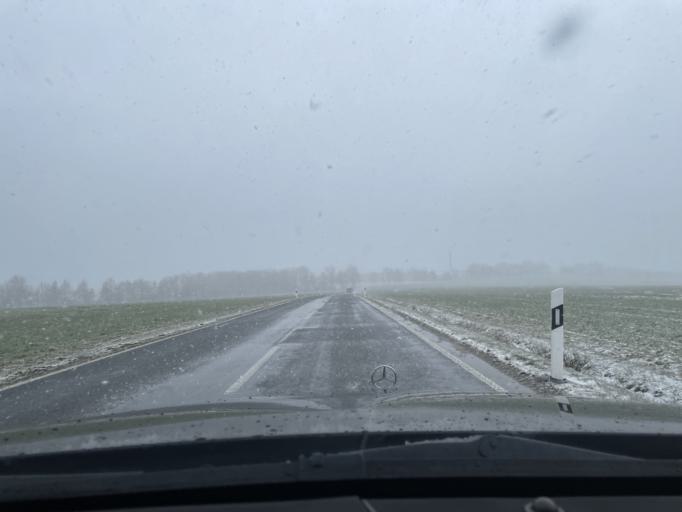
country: DE
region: Thuringia
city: Kullstedt
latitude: 51.2662
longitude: 10.2756
